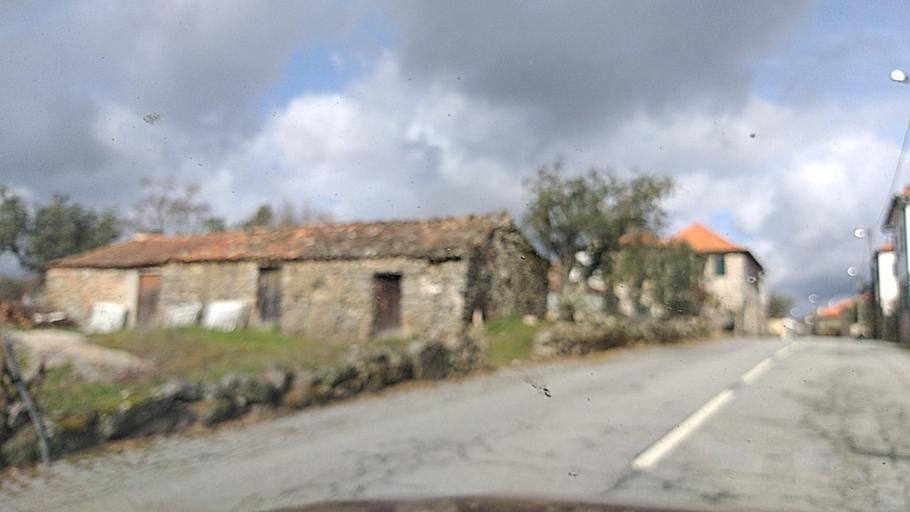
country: PT
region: Guarda
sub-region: Fornos de Algodres
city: Fornos de Algodres
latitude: 40.6492
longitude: -7.5469
